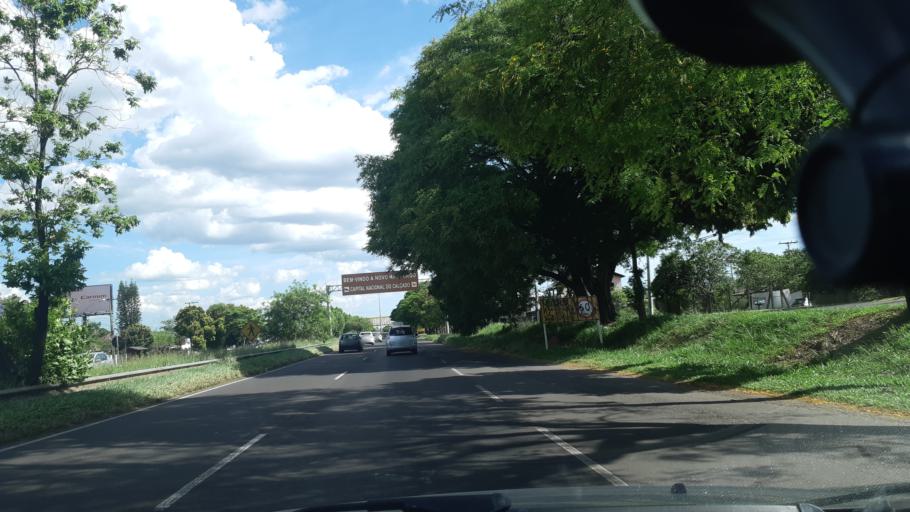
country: BR
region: Rio Grande do Sul
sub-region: Novo Hamburgo
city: Novo Hamburgo
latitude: -29.6599
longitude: -51.1441
